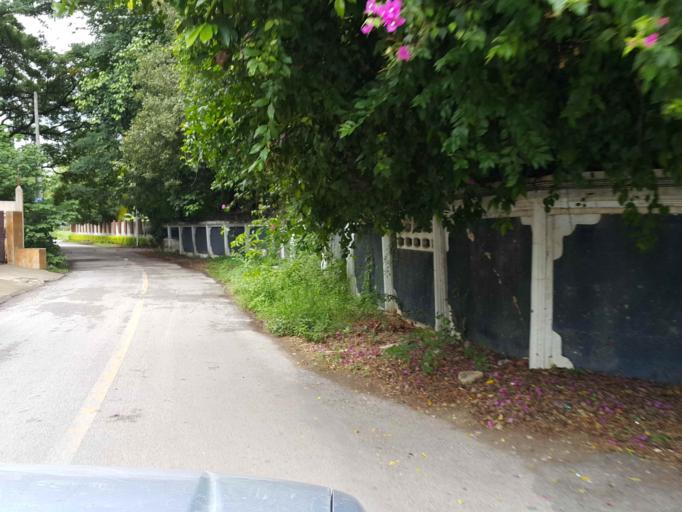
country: TH
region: Chiang Mai
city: Chiang Mai
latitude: 18.8173
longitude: 98.9949
